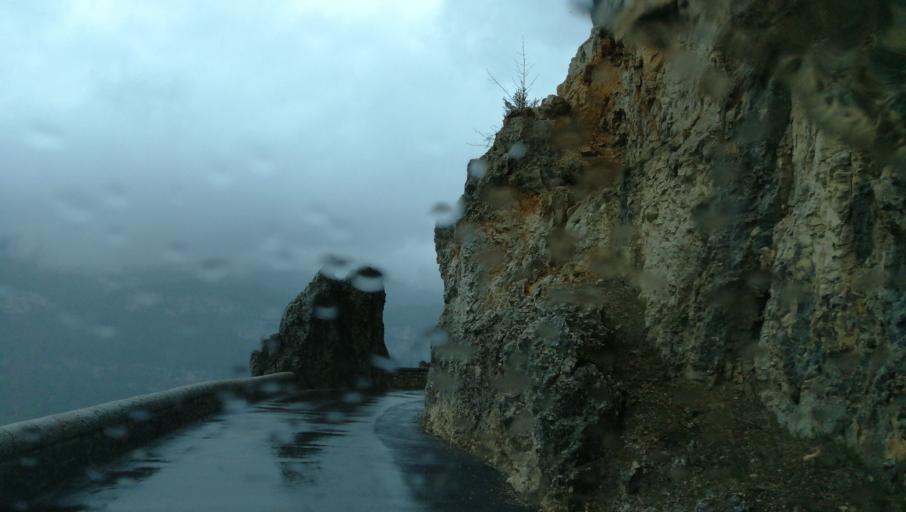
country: FR
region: Rhone-Alpes
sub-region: Departement de la Drome
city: Saint-Laurent-en-Royans
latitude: 45.0003
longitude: 5.3327
